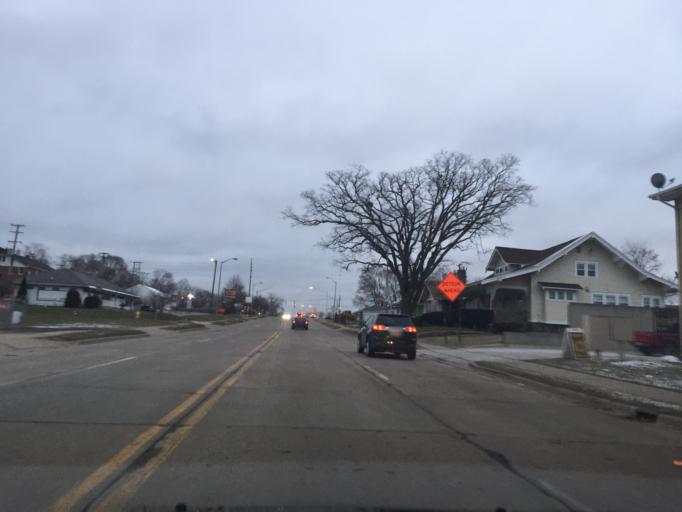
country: US
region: Michigan
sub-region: Oakland County
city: Pontiac
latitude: 42.6347
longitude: -83.2719
